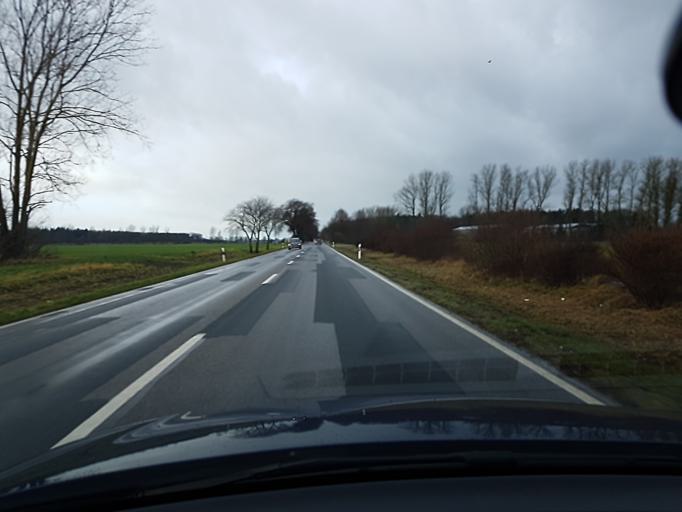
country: DE
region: Mecklenburg-Vorpommern
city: Bad Sulze
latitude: 54.0885
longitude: 12.6961
